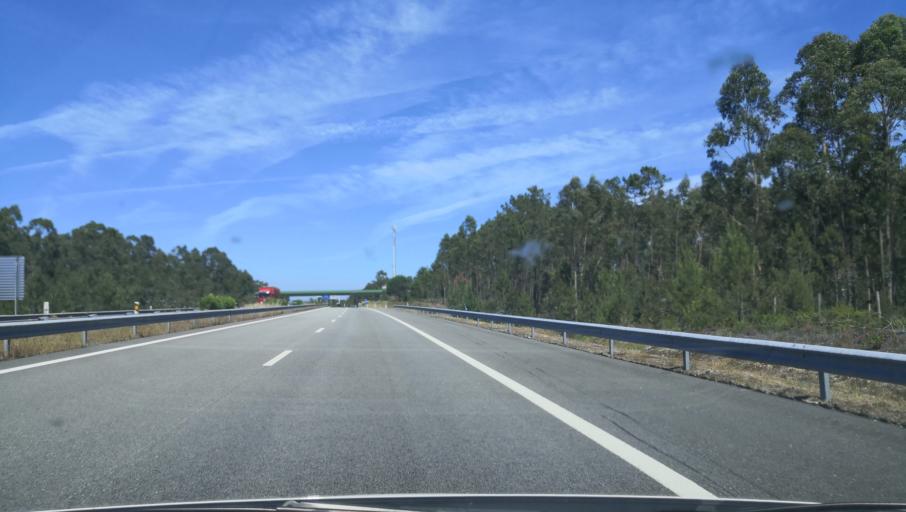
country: PT
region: Coimbra
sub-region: Montemor-O-Velho
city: Arazede
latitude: 40.2552
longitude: -8.6379
